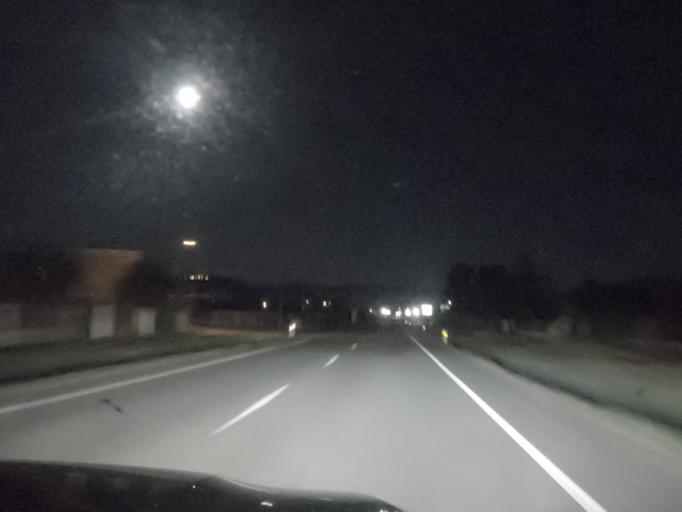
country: ES
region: Galicia
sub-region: Provincia de Ourense
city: Verin
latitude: 41.9436
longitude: -7.4728
